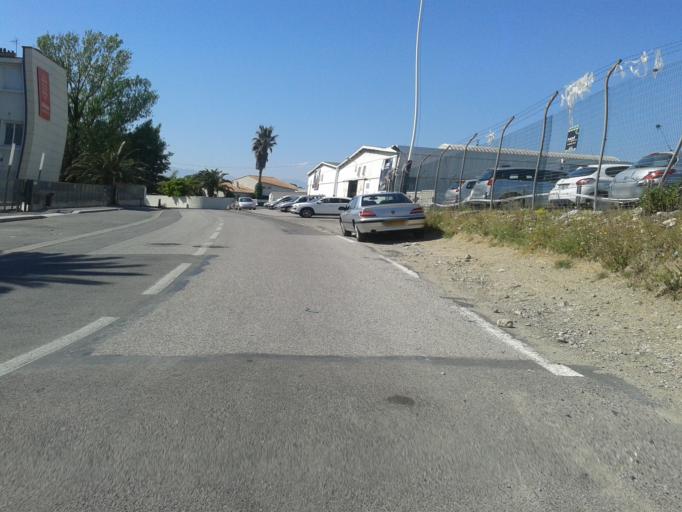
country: FR
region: Languedoc-Roussillon
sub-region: Departement des Pyrenees-Orientales
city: Perpignan
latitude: 42.6797
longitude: 2.8947
